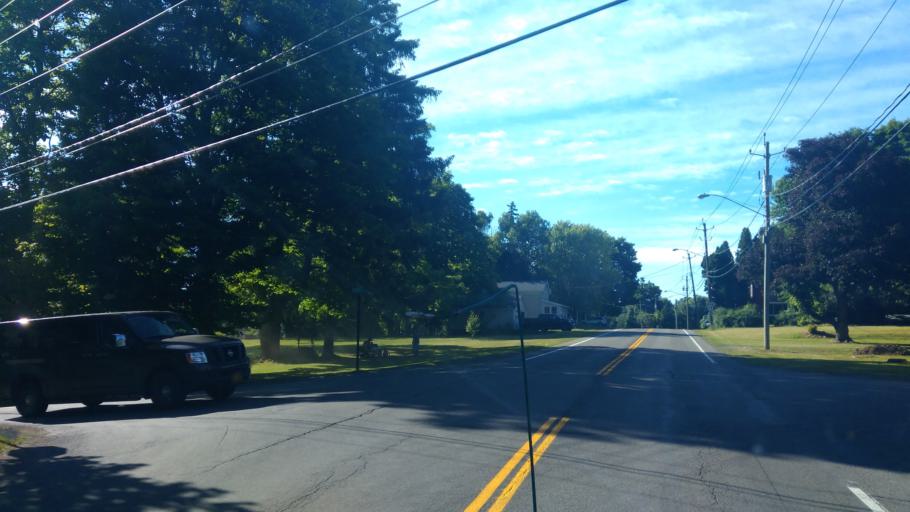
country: US
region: New York
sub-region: Wayne County
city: Lyons
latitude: 43.0234
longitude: -76.9885
